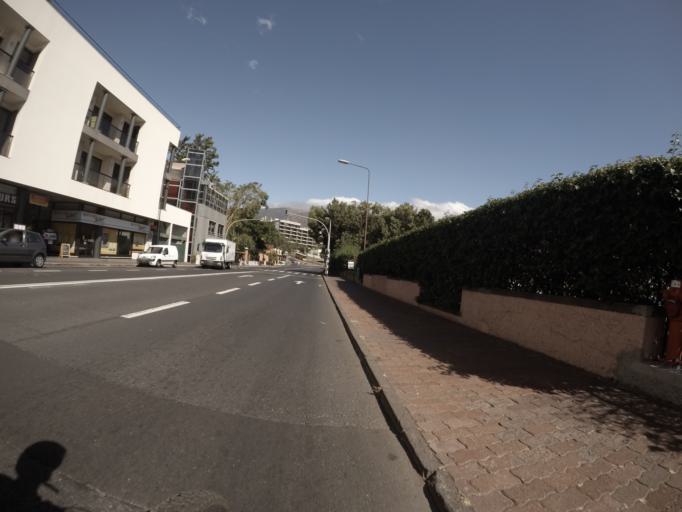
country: PT
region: Madeira
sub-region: Funchal
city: Funchal
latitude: 32.6413
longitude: -16.9240
